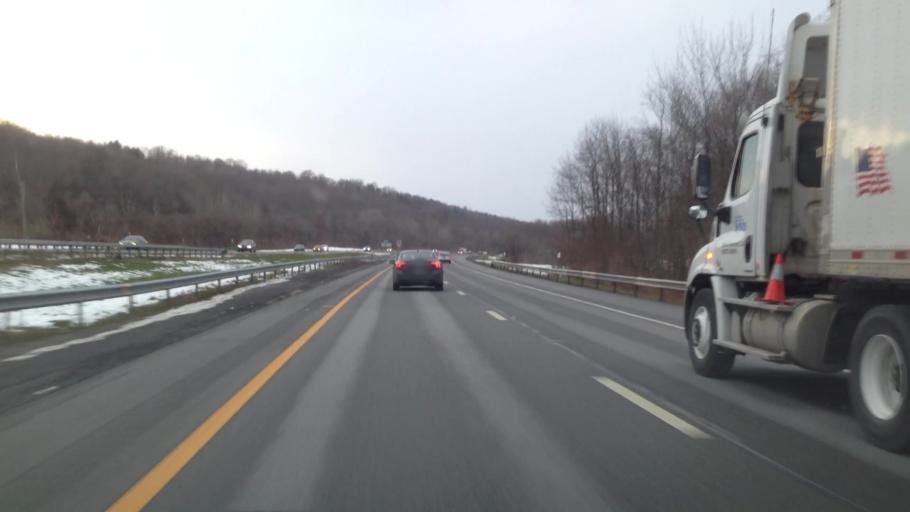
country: US
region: New York
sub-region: Montgomery County
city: Saint Johnsville
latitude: 42.9892
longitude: -74.7176
